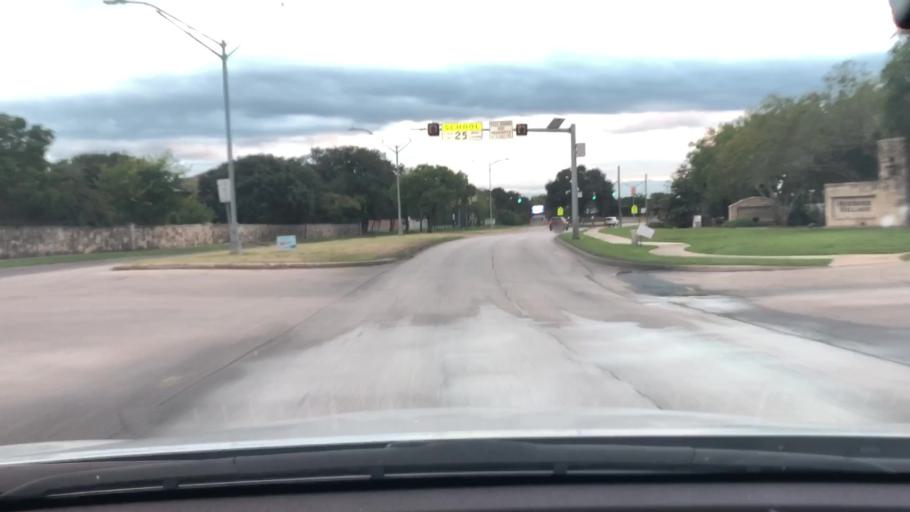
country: US
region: Texas
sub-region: Bexar County
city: Shavano Park
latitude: 29.5884
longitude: -98.5296
